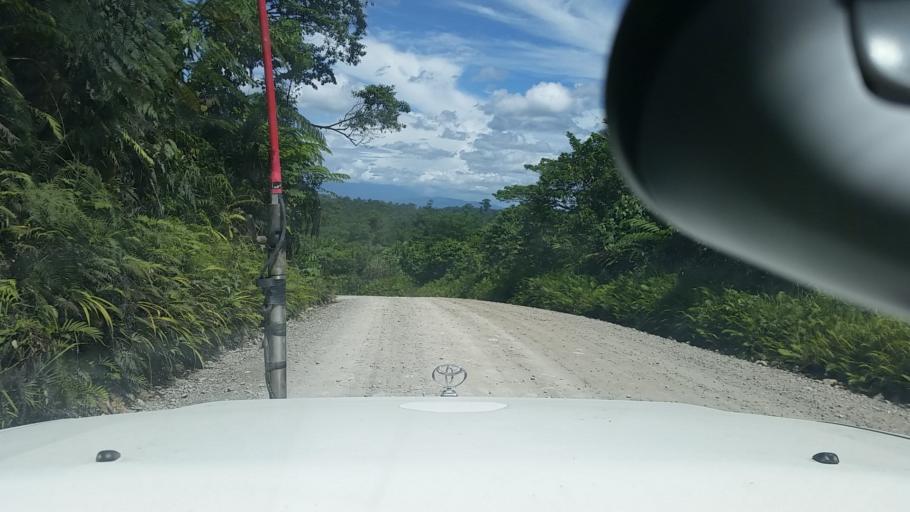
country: PG
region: Western Province
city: Kiunga
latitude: -5.5767
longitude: 141.2481
